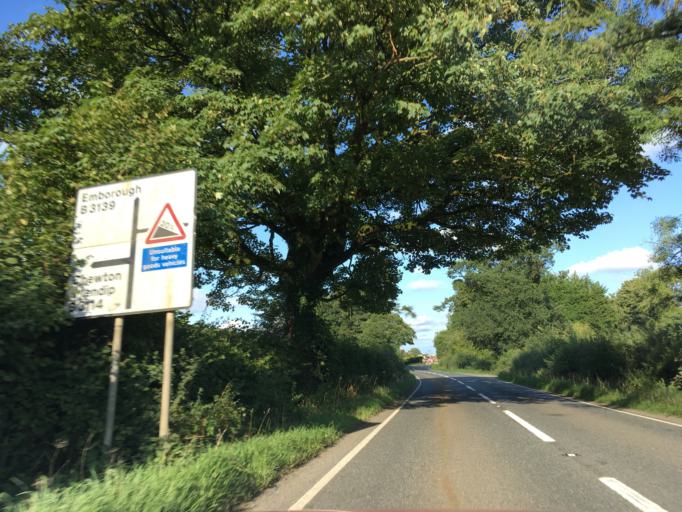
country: GB
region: England
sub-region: Somerset
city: Chilcompton
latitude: 51.2569
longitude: -2.5557
